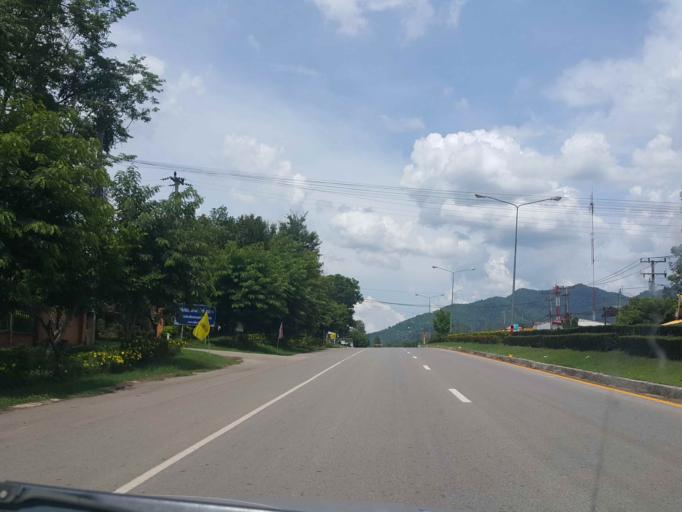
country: TH
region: Nan
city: Ban Luang
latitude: 18.8499
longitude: 100.4385
